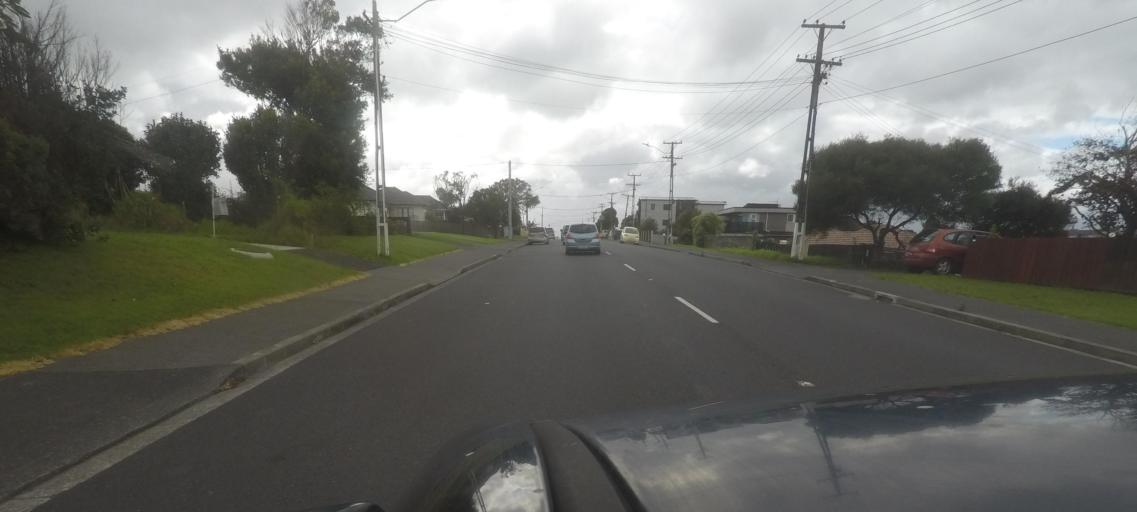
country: NZ
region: Auckland
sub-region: Auckland
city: Auckland
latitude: -36.9100
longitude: 174.7255
